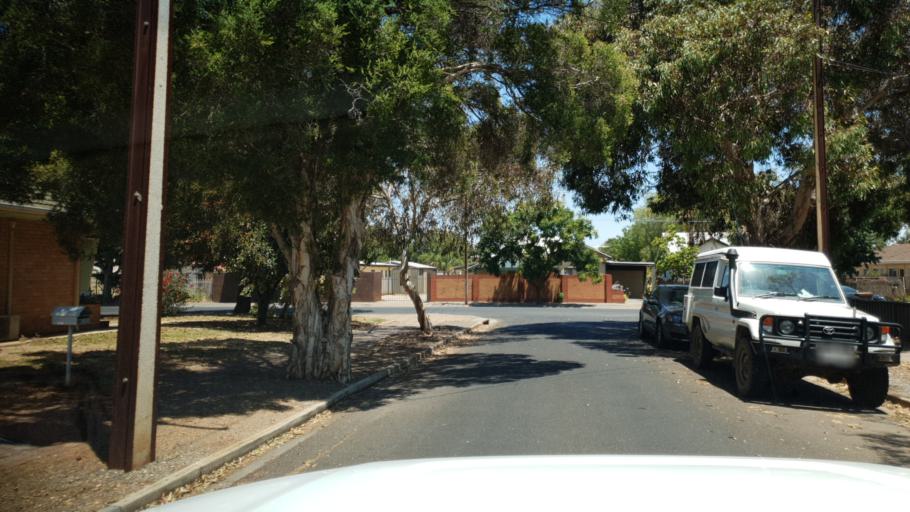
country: AU
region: South Australia
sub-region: Mitcham
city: Clarence Gardens
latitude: -34.9788
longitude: 138.5832
